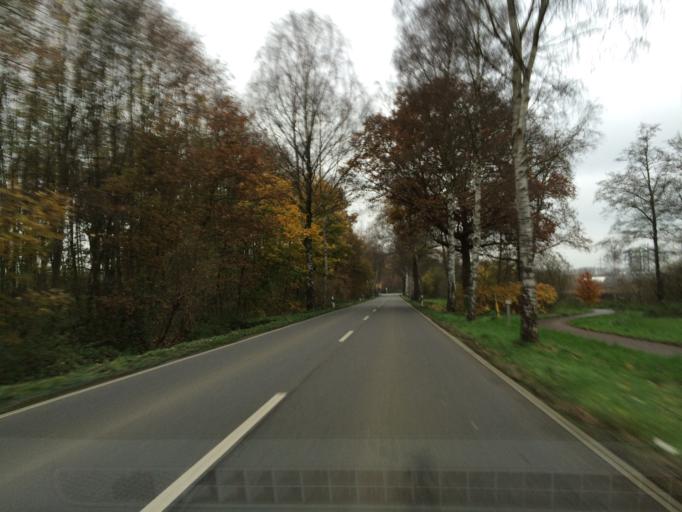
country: DE
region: North Rhine-Westphalia
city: Marl
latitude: 51.6608
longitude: 7.0382
